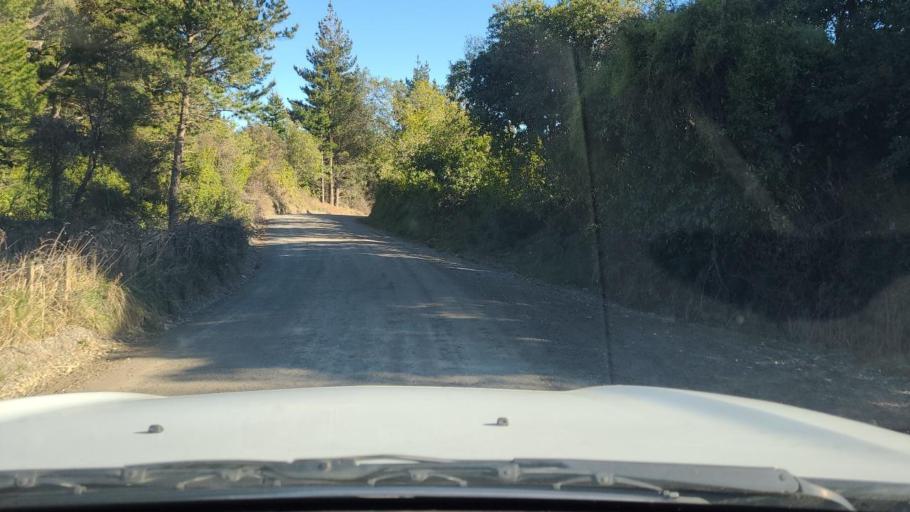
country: NZ
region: Hawke's Bay
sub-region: Napier City
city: Taradale
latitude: -39.3595
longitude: 176.5395
